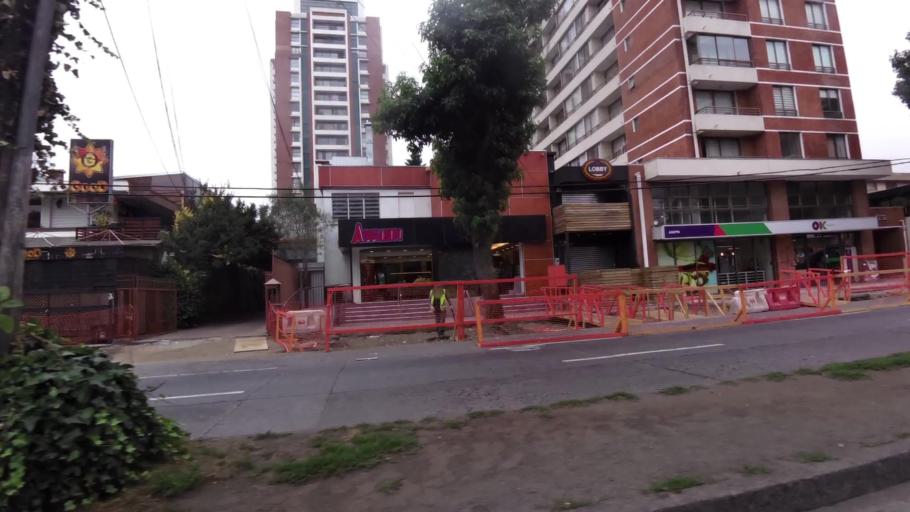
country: CL
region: Biobio
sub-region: Provincia de Concepcion
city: Concepcion
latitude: -36.8274
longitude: -73.0405
